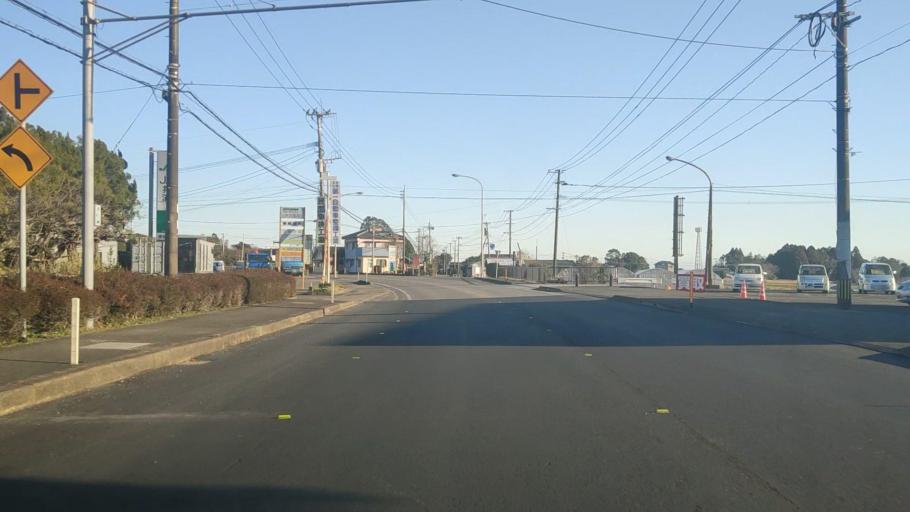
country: JP
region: Miyazaki
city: Takanabe
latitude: 32.2306
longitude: 131.5480
